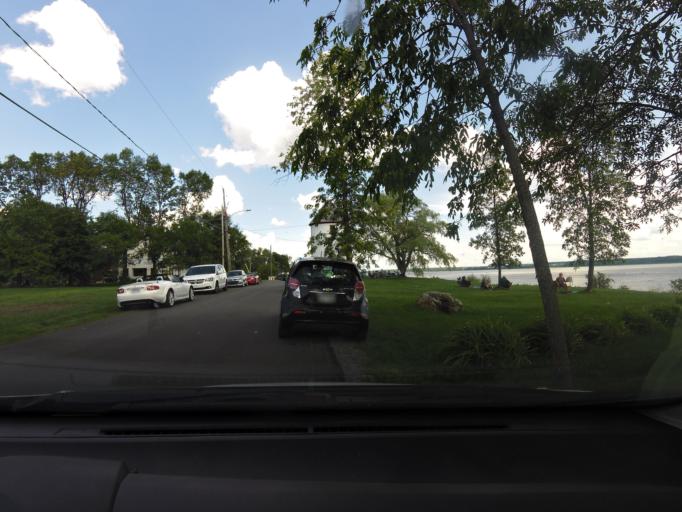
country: CA
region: Quebec
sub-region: Capitale-Nationale
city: Saint-Marc-des-Carrieres
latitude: 46.5878
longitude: -72.0384
